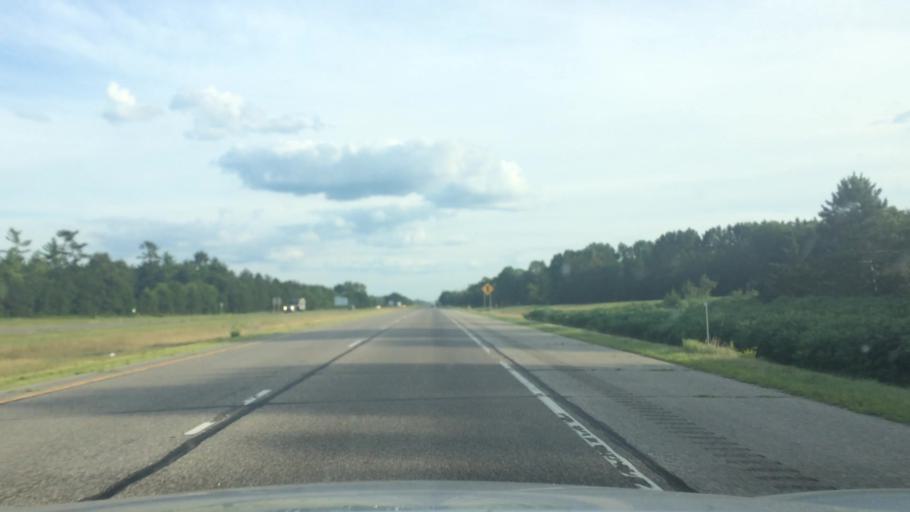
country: US
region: Wisconsin
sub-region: Portage County
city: Plover
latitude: 44.3089
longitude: -89.5236
